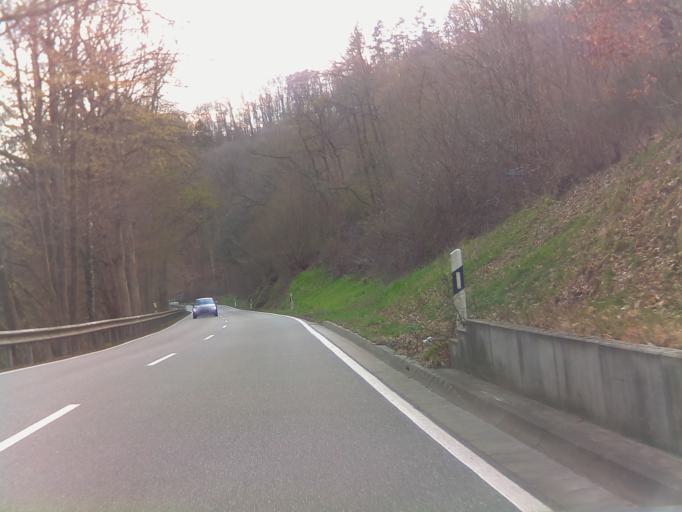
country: DE
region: Rheinland-Pfalz
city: Lauschied
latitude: 49.7568
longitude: 7.6142
